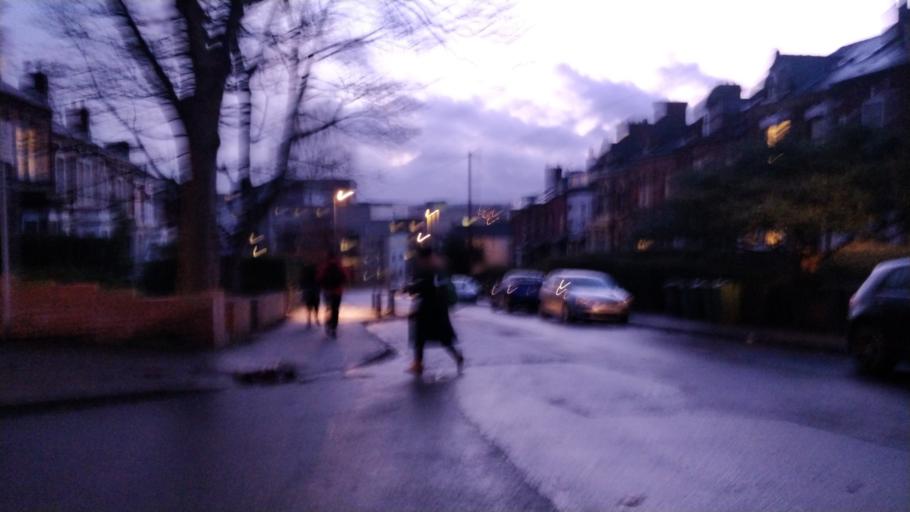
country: GB
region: England
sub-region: City and Borough of Leeds
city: Leeds
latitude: 53.8029
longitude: -1.5626
